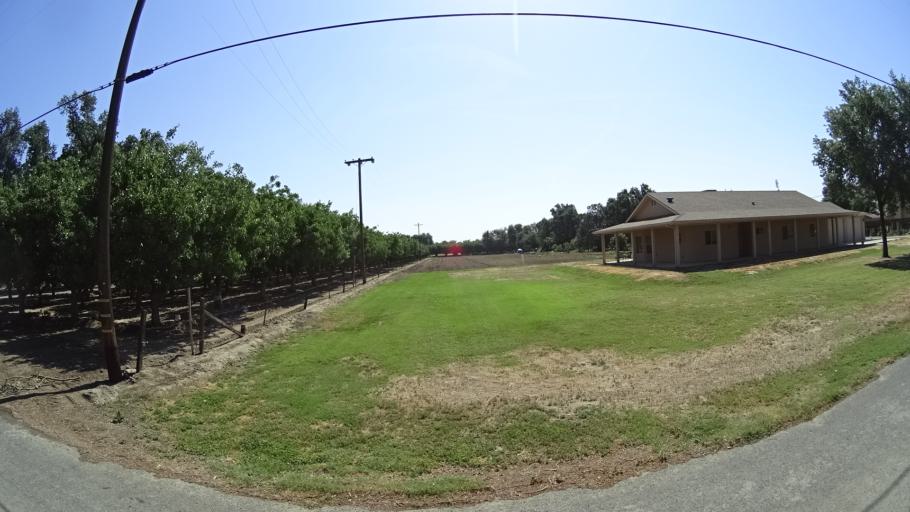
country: US
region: California
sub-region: Kings County
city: Lemoore
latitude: 36.3526
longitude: -119.8250
